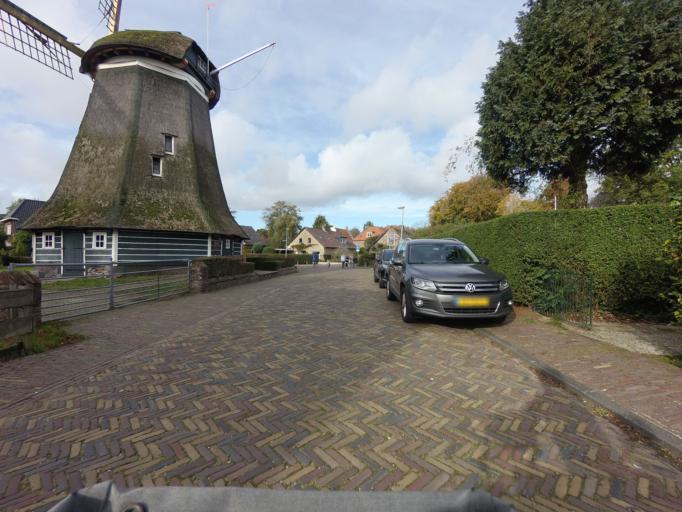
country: NL
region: North Holland
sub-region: Gemeente Laren
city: Laren
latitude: 52.2539
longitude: 5.2218
